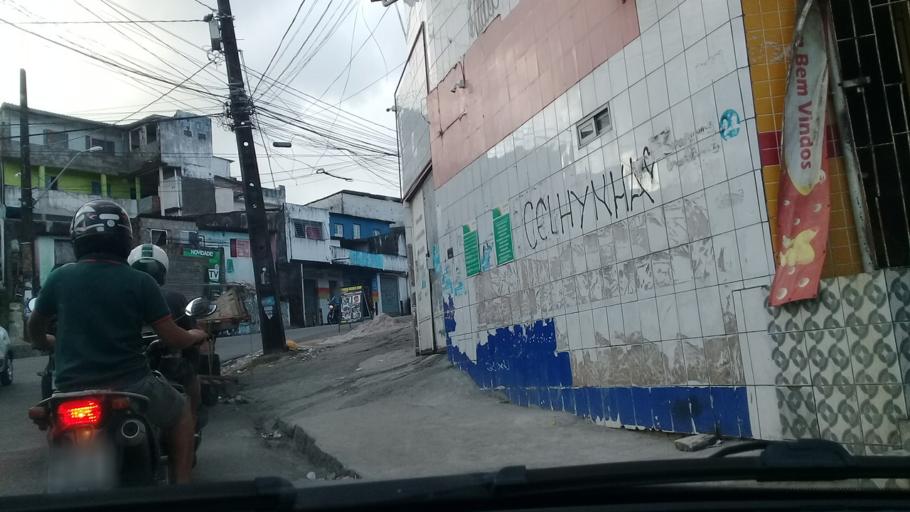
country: BR
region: Pernambuco
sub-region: Jaboatao Dos Guararapes
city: Jaboatao dos Guararapes
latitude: -8.1321
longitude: -34.9494
